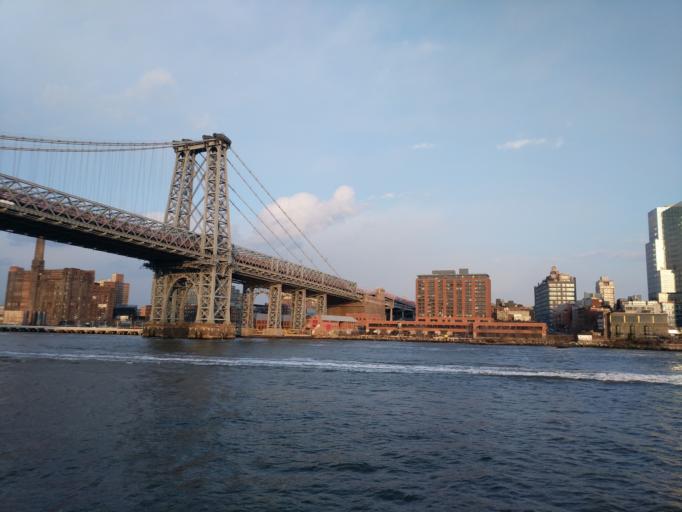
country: US
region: New York
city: New York City
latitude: 40.7119
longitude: -73.9725
